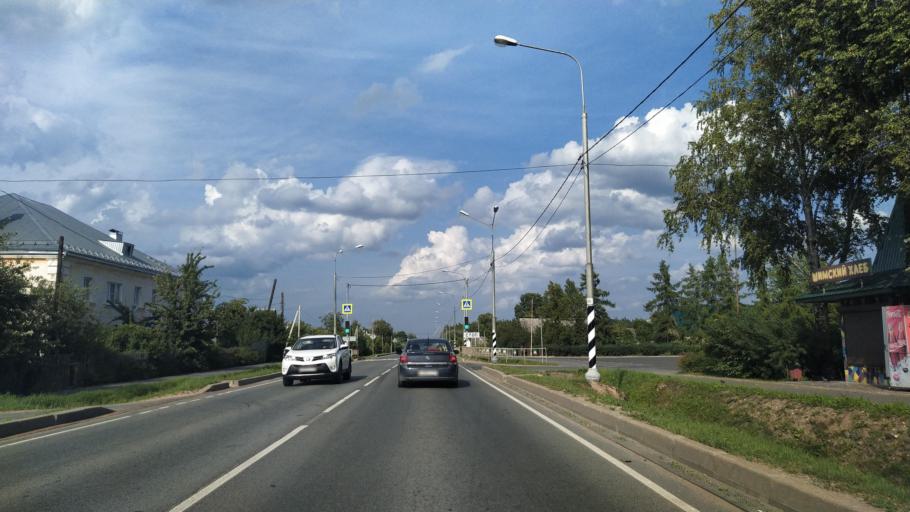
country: RU
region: Novgorod
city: Shimsk
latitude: 58.2113
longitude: 30.7235
